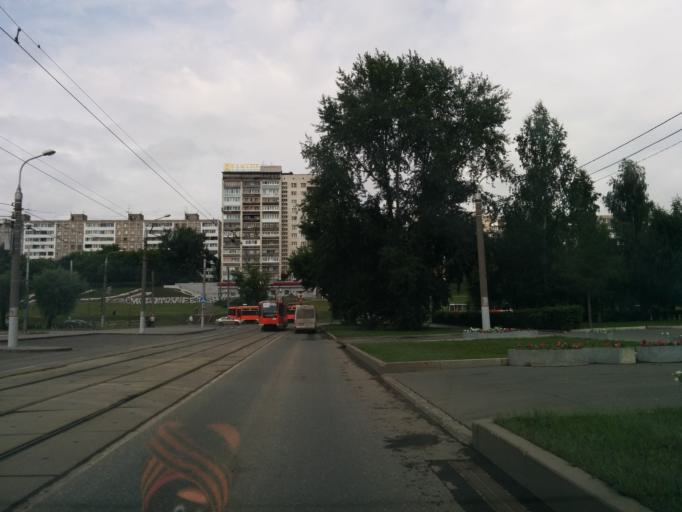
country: RU
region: Perm
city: Perm
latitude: 58.0086
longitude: 56.2196
